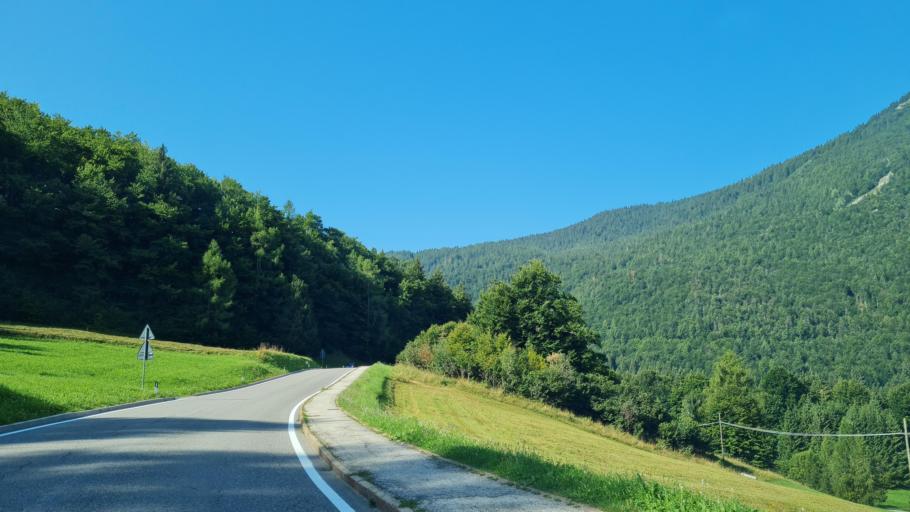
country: IT
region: Trentino-Alto Adige
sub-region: Provincia di Trento
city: Centa San Nicolo
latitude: 45.9386
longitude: 11.2290
